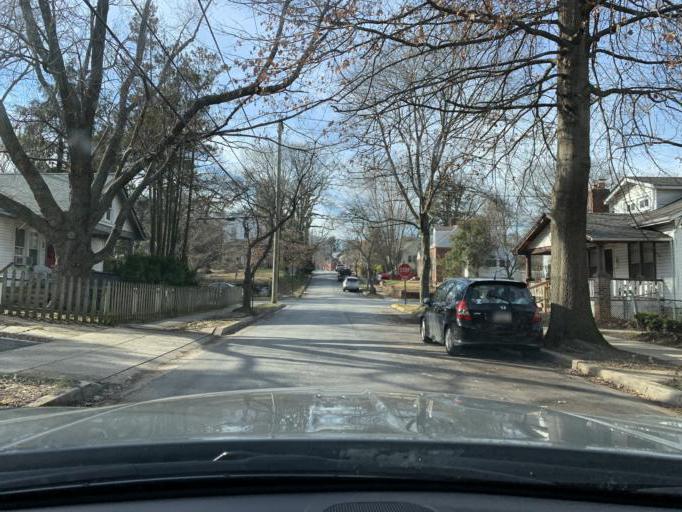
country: US
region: Maryland
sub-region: Prince George's County
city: Mount Rainier
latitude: 38.9412
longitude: -76.9655
